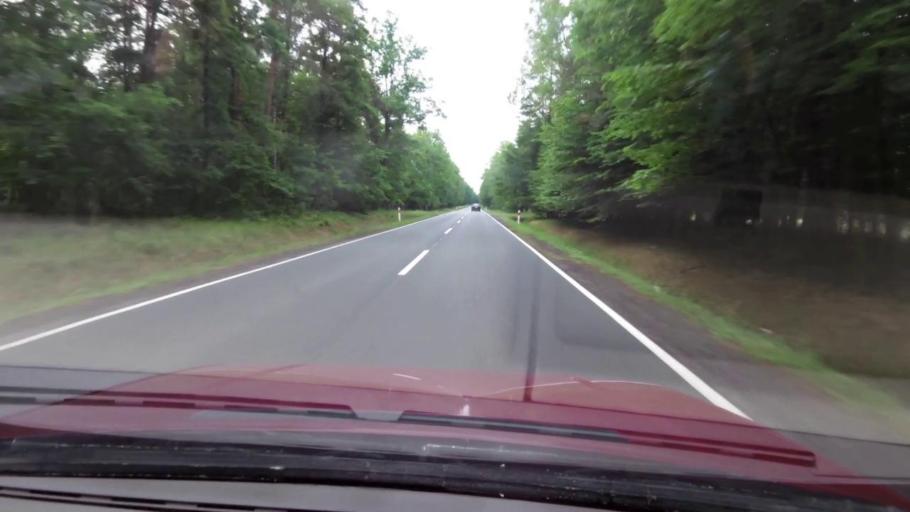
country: PL
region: Pomeranian Voivodeship
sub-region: Powiat bytowski
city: Trzebielino
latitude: 54.2231
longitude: 17.0876
